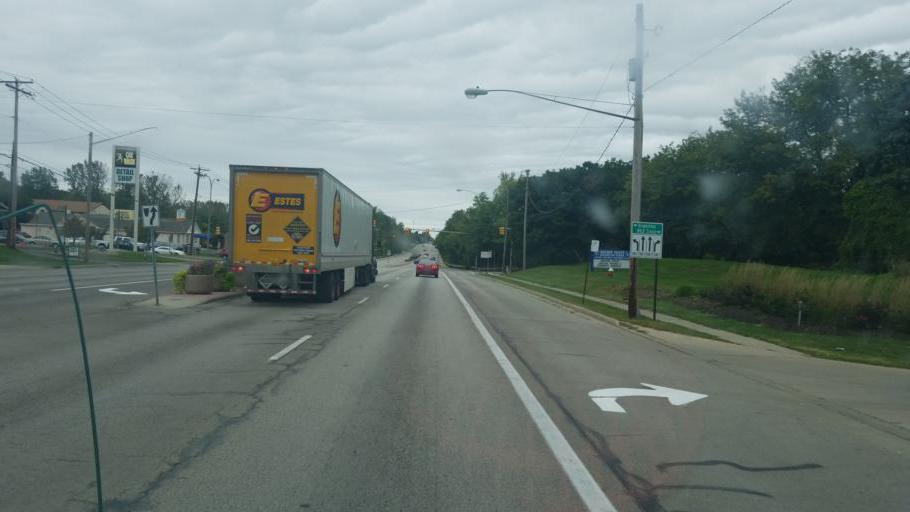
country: US
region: Ohio
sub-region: Lucas County
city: Maumee
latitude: 41.6070
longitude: -83.6646
